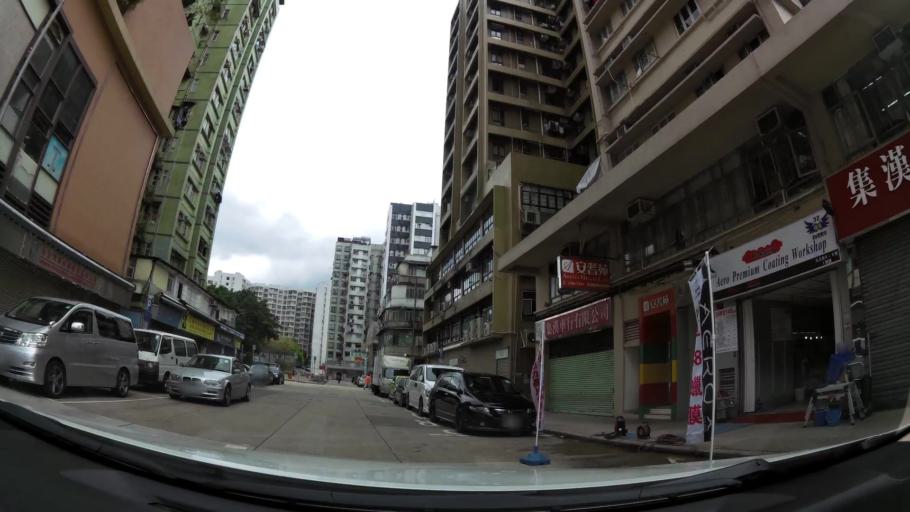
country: HK
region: Sham Shui Po
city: Sham Shui Po
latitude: 22.3290
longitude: 114.1568
